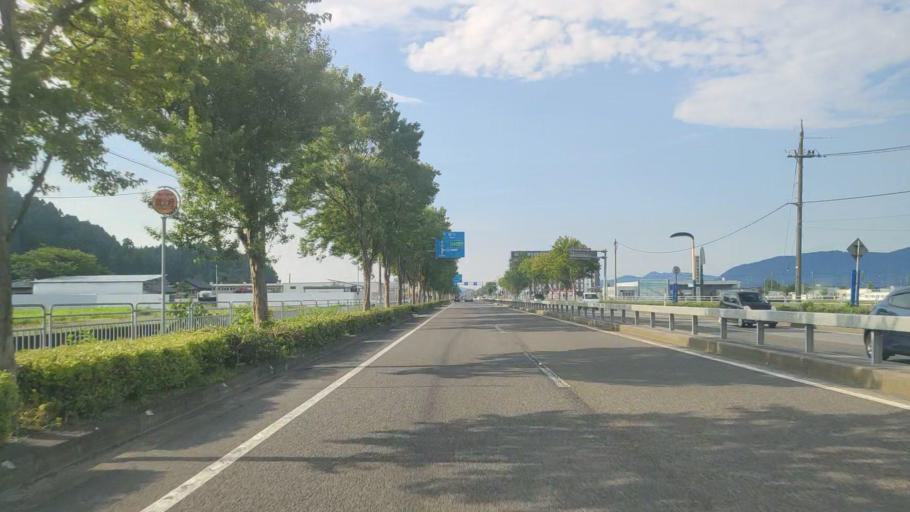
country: JP
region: Fukui
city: Takefu
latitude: 35.8994
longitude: 136.1923
